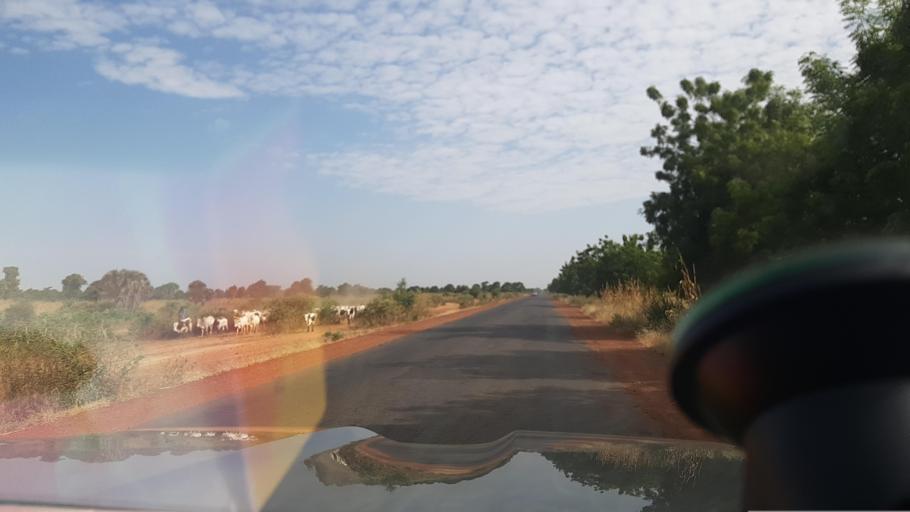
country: ML
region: Segou
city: Segou
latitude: 13.5059
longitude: -6.1467
